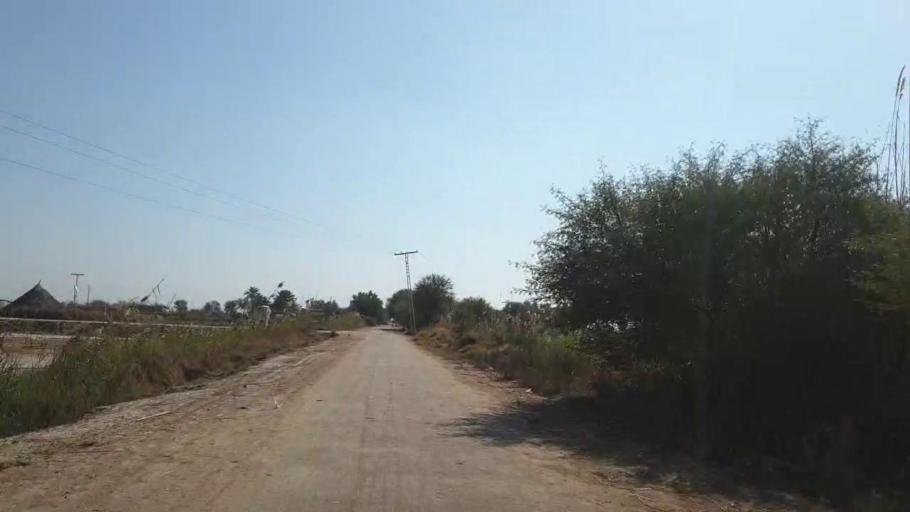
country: PK
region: Sindh
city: Mirpur Khas
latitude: 25.6399
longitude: 69.0280
